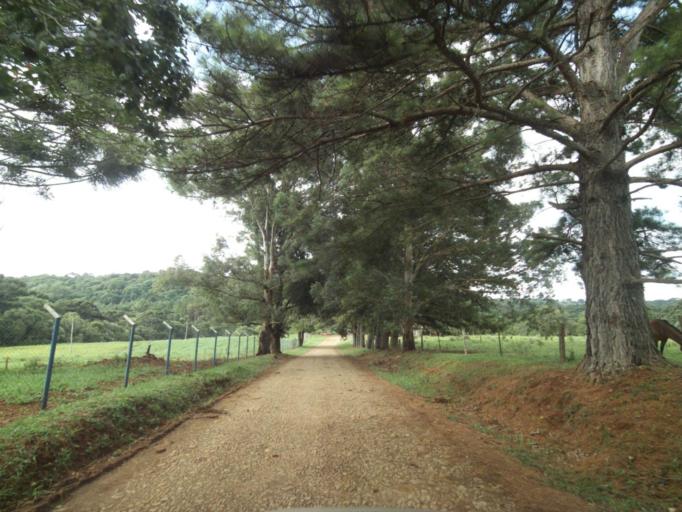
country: BR
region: Rio Grande do Sul
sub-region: Lagoa Vermelha
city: Lagoa Vermelha
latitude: -28.2043
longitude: -51.5422
